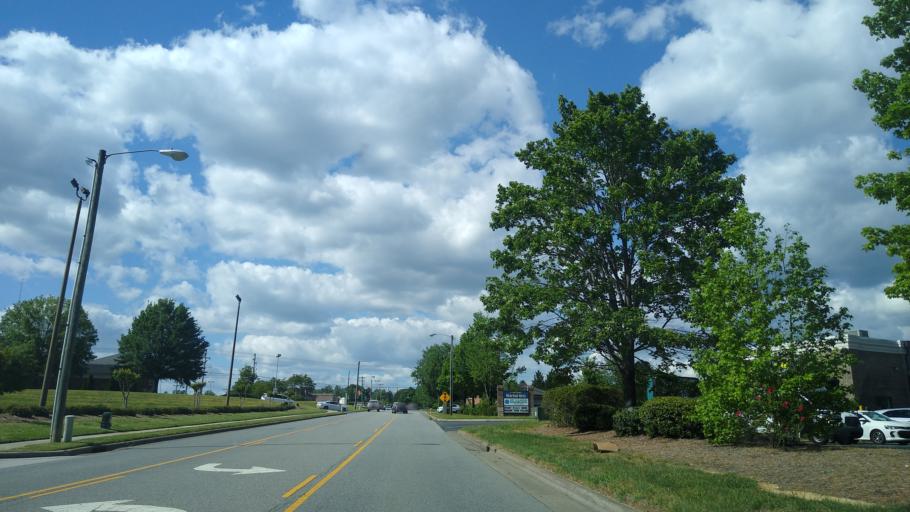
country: US
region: North Carolina
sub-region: Forsyth County
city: Kernersville
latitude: 36.1058
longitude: -80.0982
